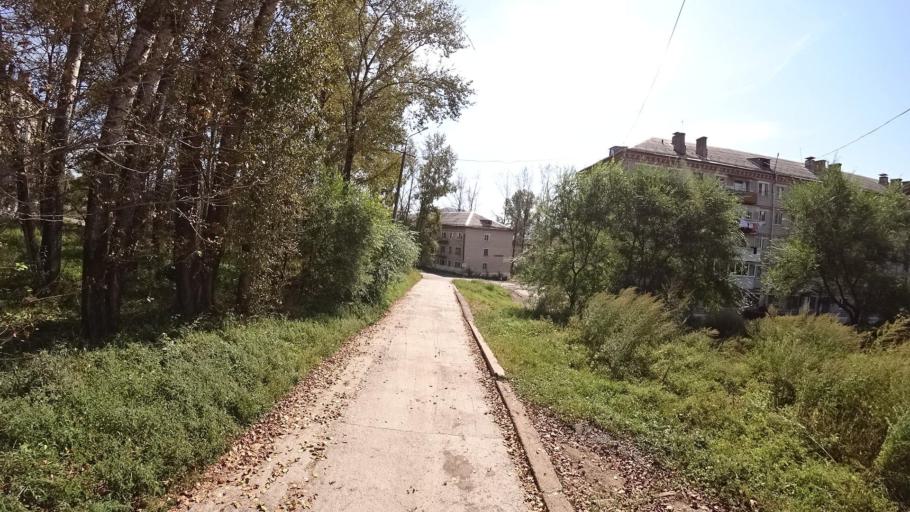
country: RU
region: Jewish Autonomous Oblast
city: Londoko
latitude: 49.0138
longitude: 131.8860
